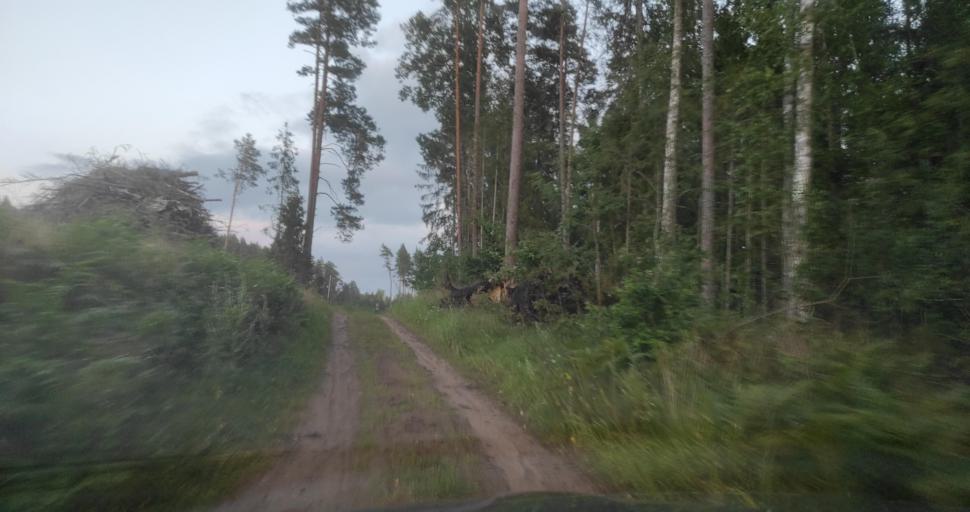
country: LV
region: Kuldigas Rajons
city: Kuldiga
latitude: 57.0662
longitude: 21.8604
